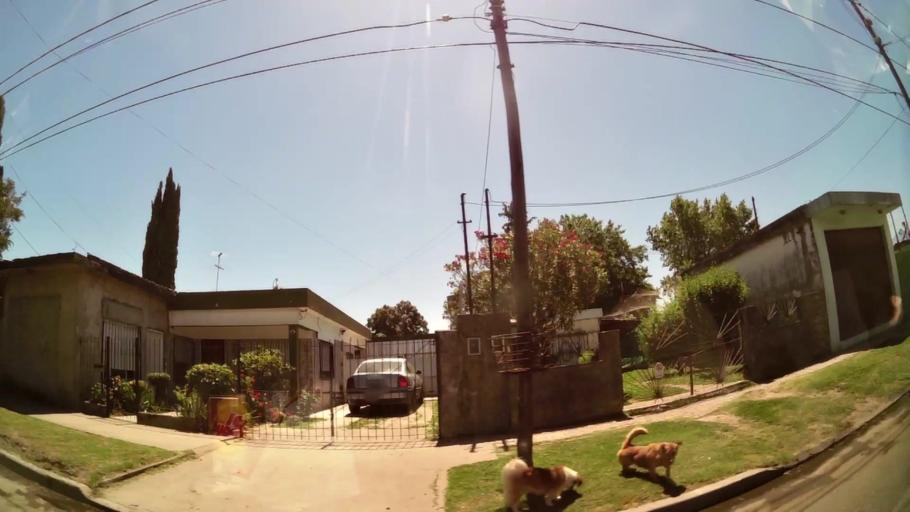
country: AR
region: Buenos Aires
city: Hurlingham
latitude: -34.4899
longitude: -58.6663
